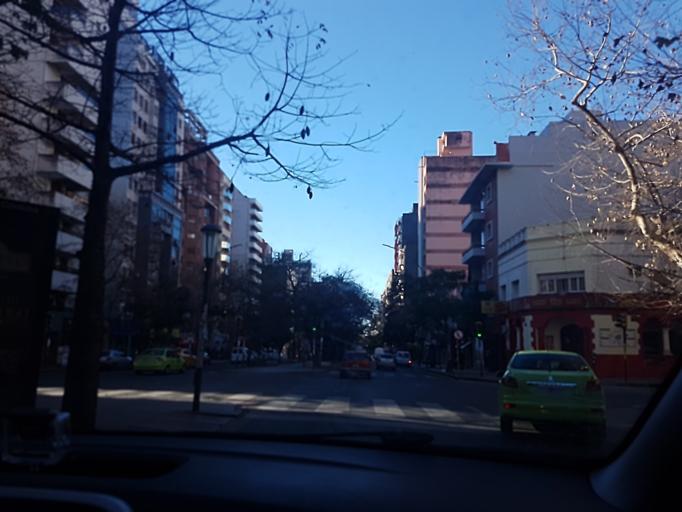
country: AR
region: Cordoba
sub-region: Departamento de Capital
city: Cordoba
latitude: -31.4235
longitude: -64.1826
